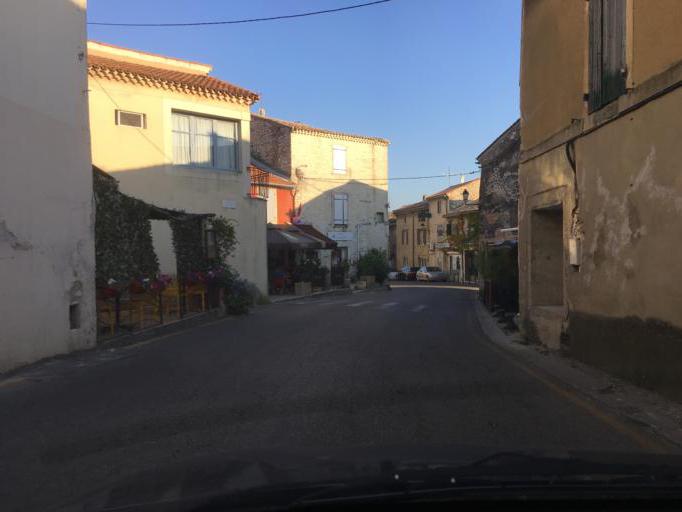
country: FR
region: Languedoc-Roussillon
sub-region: Departement du Gard
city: Tavel
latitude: 44.0118
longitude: 4.7003
